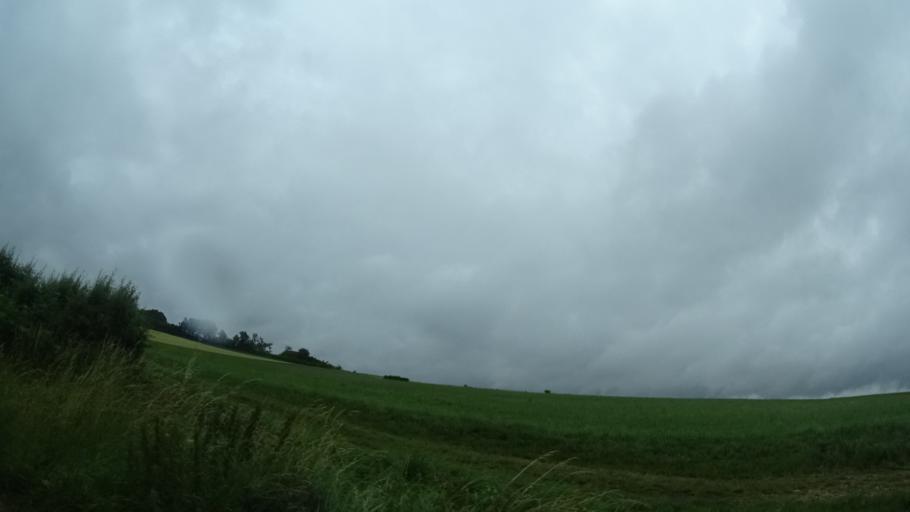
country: LU
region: Luxembourg
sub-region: Canton de Capellen
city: Clemency
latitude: 49.5970
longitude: 5.8601
